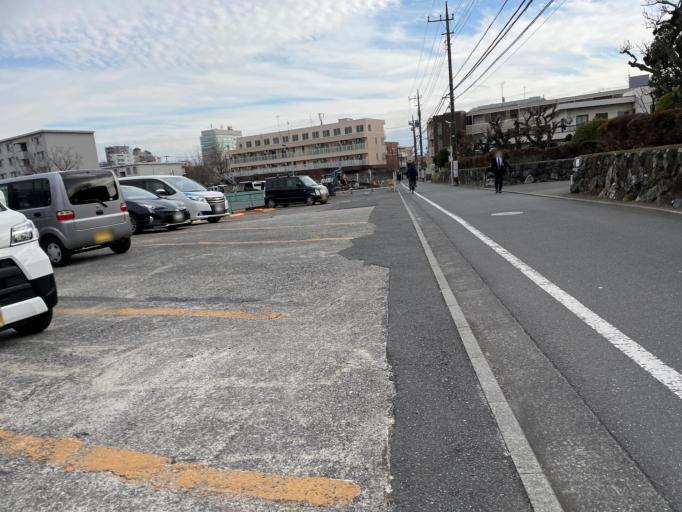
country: JP
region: Tokyo
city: Kamirenjaku
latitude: 35.7056
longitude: 139.5394
